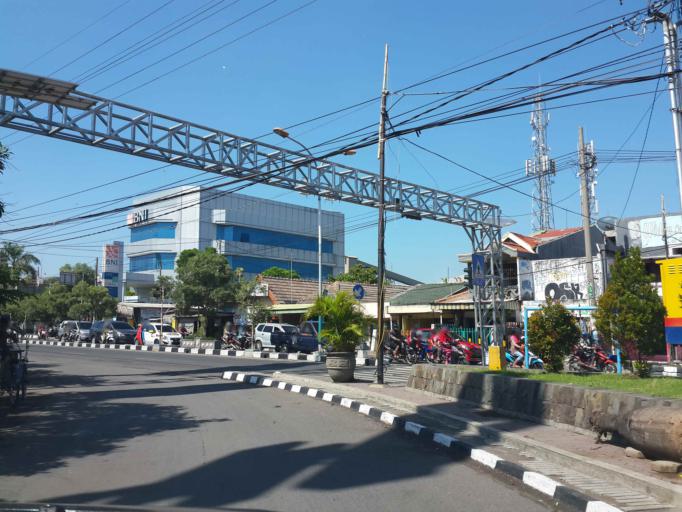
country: ID
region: East Java
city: Gresik
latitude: -7.1714
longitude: 112.6537
